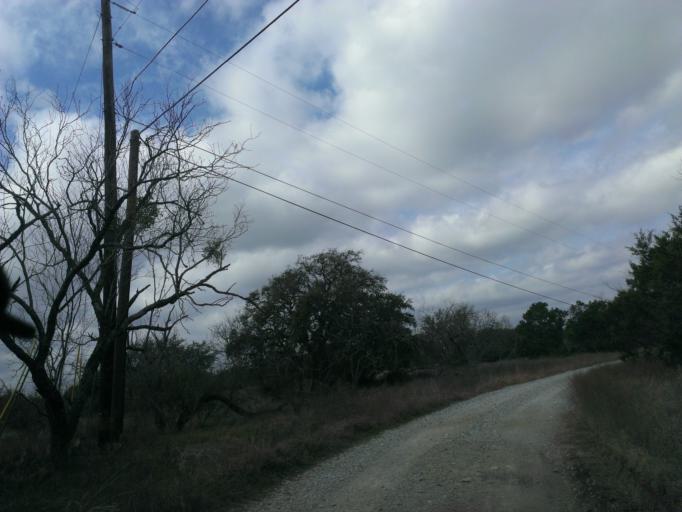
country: US
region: Texas
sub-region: Travis County
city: Briarcliff
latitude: 30.3890
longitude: -98.0917
